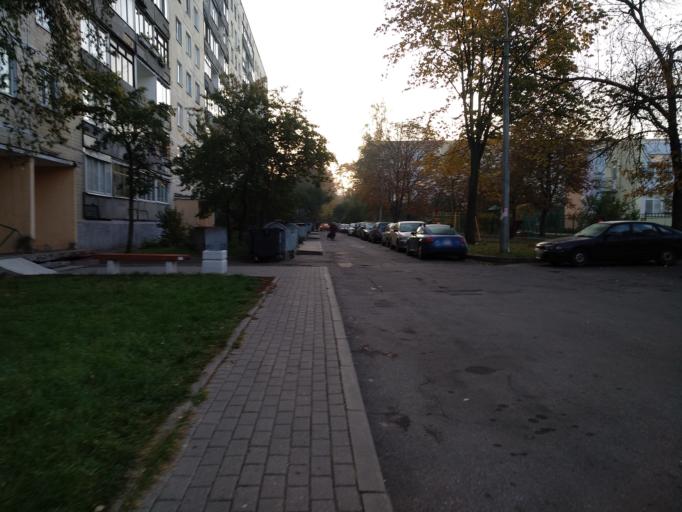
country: BY
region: Minsk
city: Minsk
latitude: 53.9294
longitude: 27.5776
